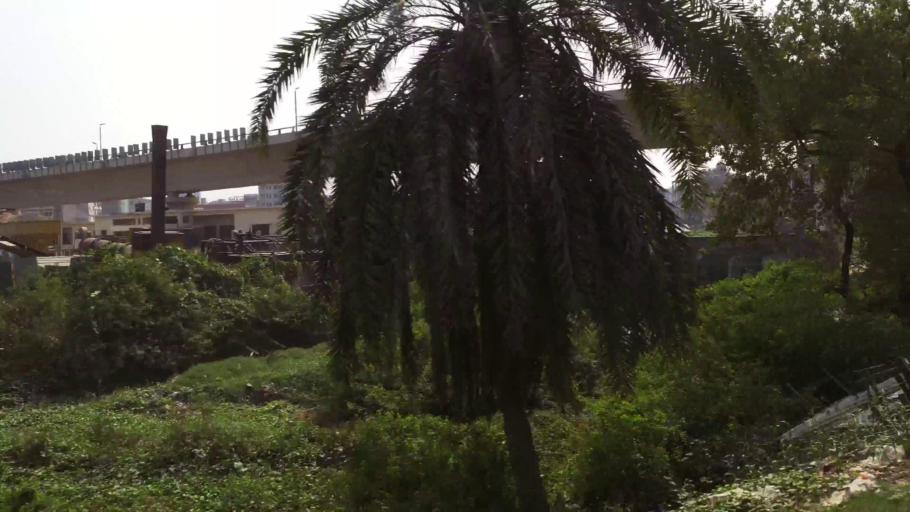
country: BD
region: Dhaka
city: Tungi
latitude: 23.8772
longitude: 90.4059
